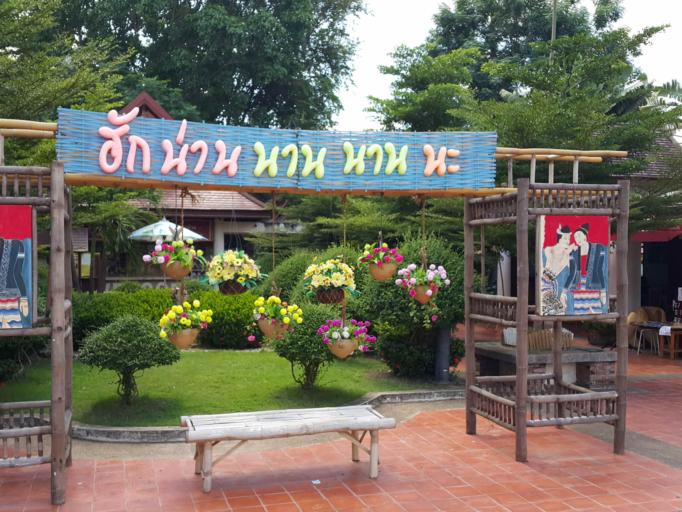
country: TH
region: Nan
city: Nan
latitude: 18.7750
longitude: 100.7720
